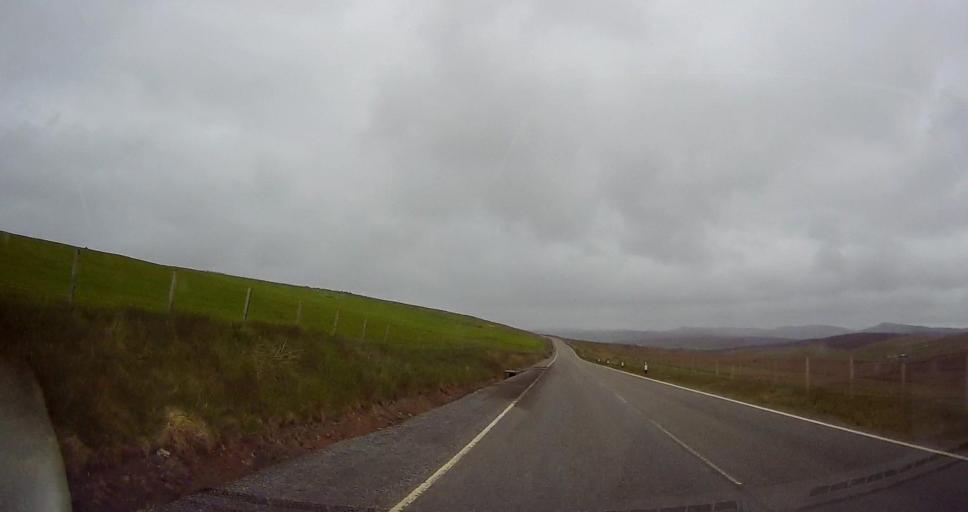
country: GB
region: Scotland
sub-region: Shetland Islands
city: Lerwick
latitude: 60.2647
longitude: -1.3980
